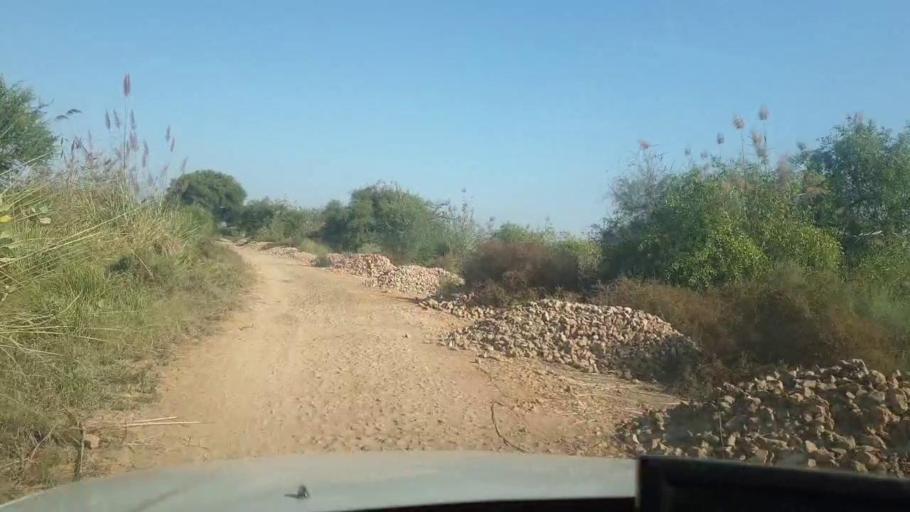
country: PK
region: Sindh
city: Mirpur Sakro
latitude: 24.5027
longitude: 67.6231
